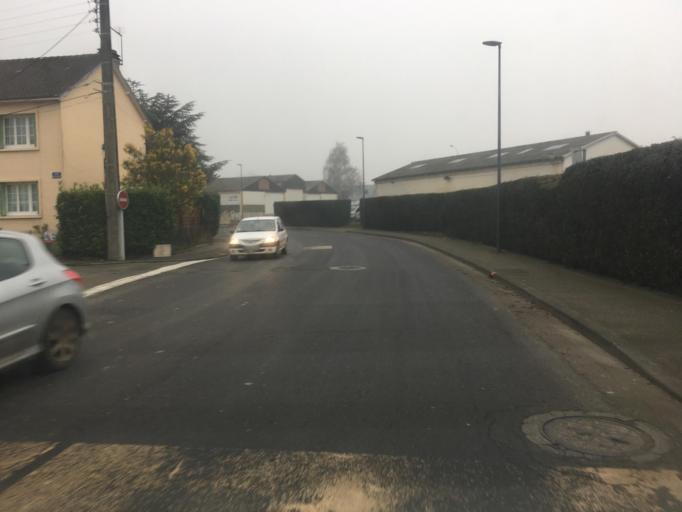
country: FR
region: Haute-Normandie
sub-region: Departement de la Seine-Maritime
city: Neufchatel-en-Bray
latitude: 49.7304
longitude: 1.4375
